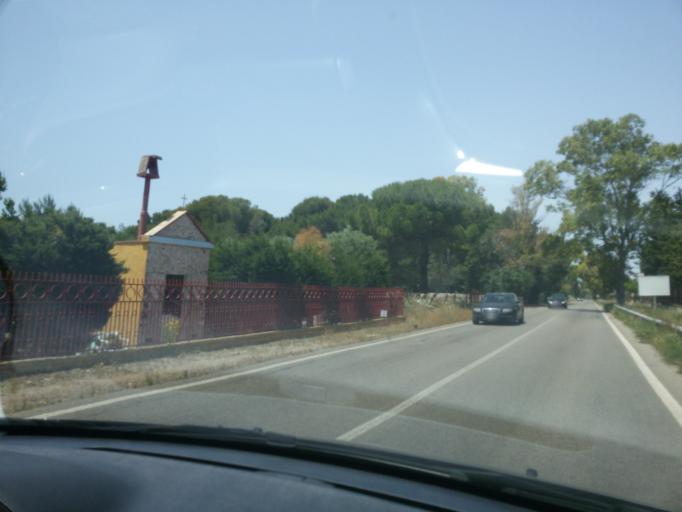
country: IT
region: Apulia
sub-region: Provincia di Lecce
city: Porto Cesareo
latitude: 40.2601
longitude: 17.9221
